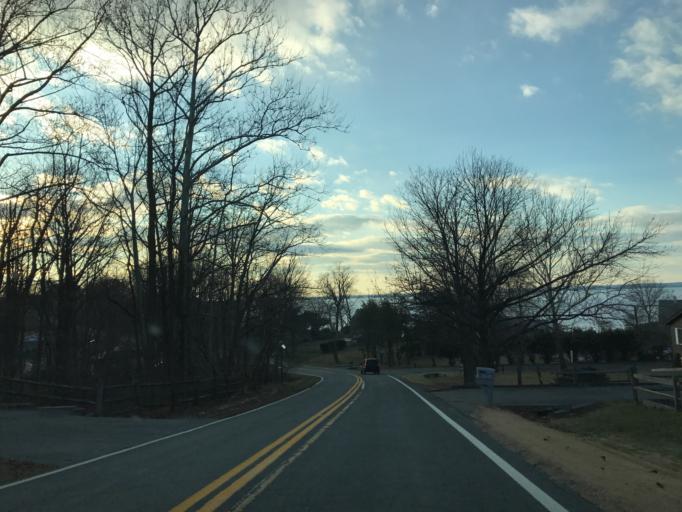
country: US
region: Maryland
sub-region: Cecil County
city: Charlestown
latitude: 39.4623
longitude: -76.0004
